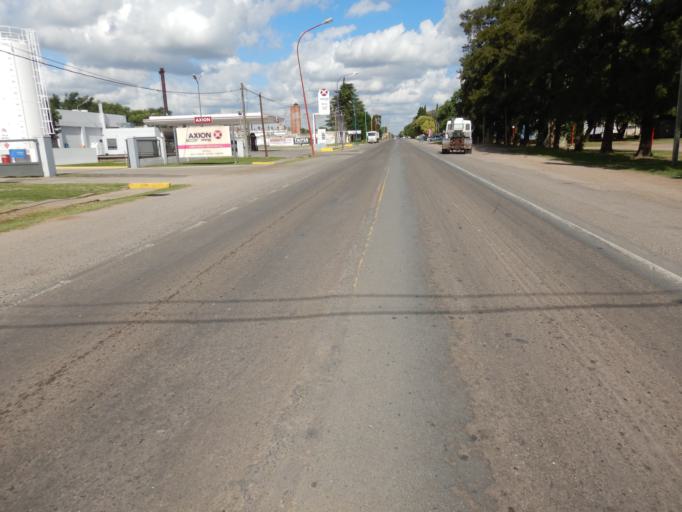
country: AR
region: Santa Fe
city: Canada de Gomez
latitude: -32.8083
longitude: -61.4066
